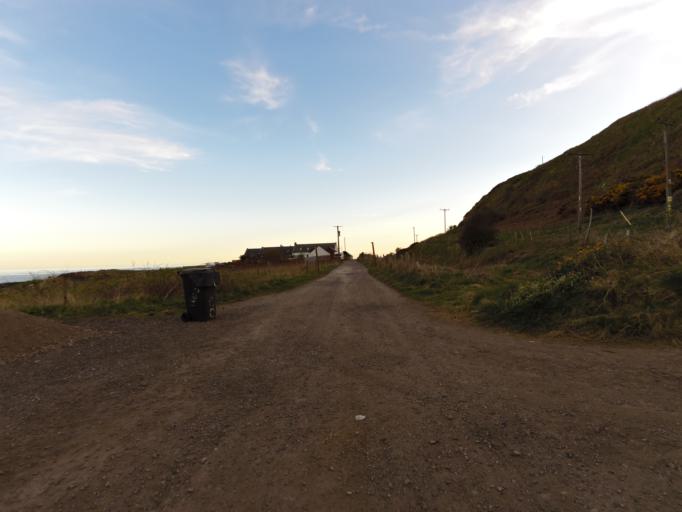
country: GB
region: Scotland
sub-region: Aberdeenshire
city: Inverbervie
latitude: 56.8259
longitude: -2.2916
